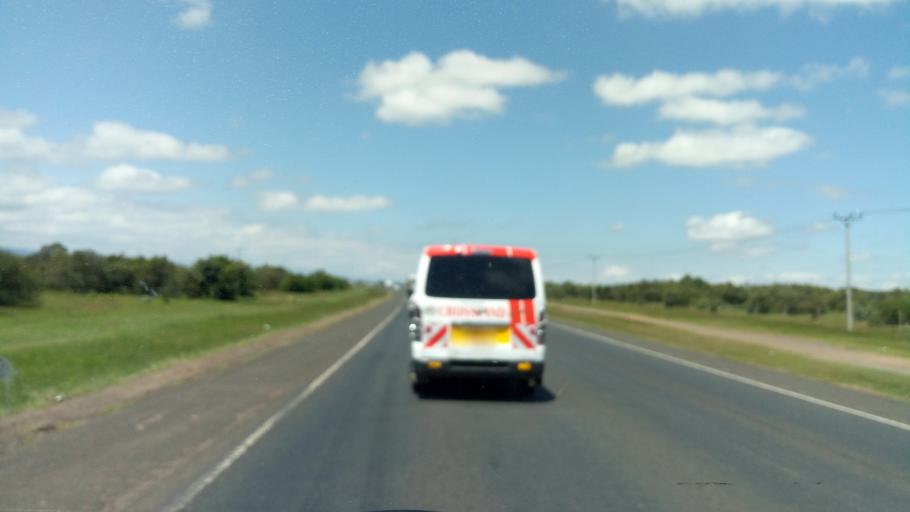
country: KE
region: Nakuru
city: Naivasha
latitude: -0.5339
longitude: 36.3335
